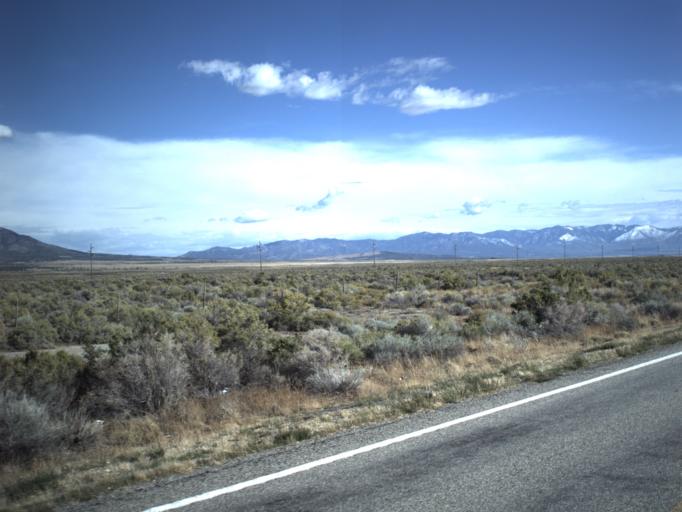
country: US
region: Utah
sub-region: Millard County
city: Delta
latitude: 39.2803
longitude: -112.4599
